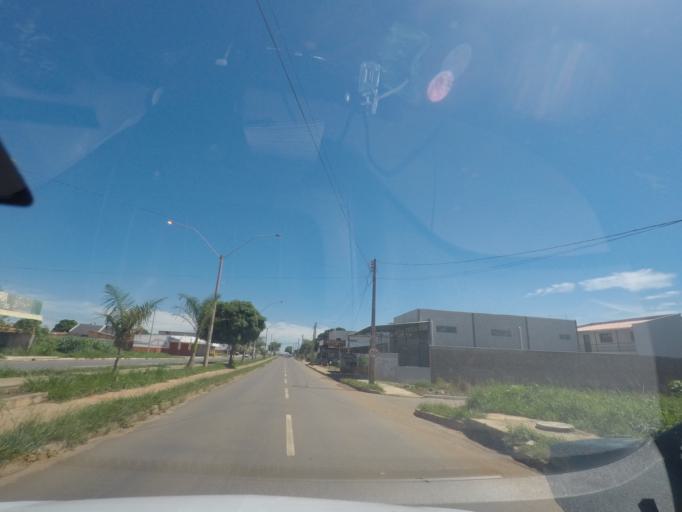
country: BR
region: Goias
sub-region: Aparecida De Goiania
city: Aparecida de Goiania
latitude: -16.7861
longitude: -49.3308
